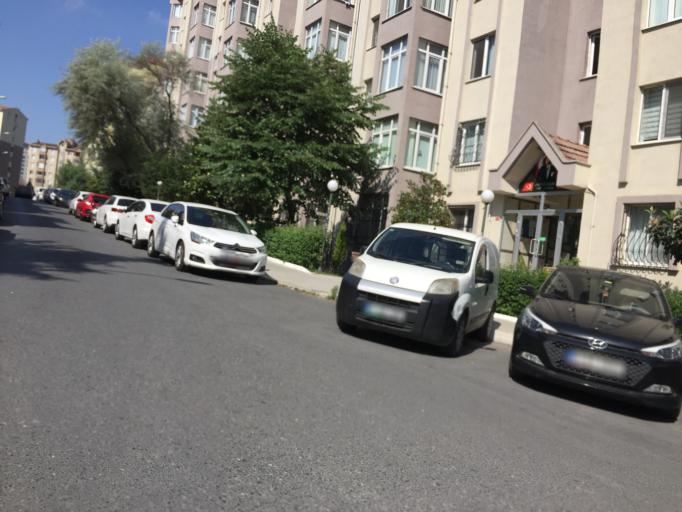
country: TR
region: Istanbul
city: Esenyurt
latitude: 41.0627
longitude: 28.6747
